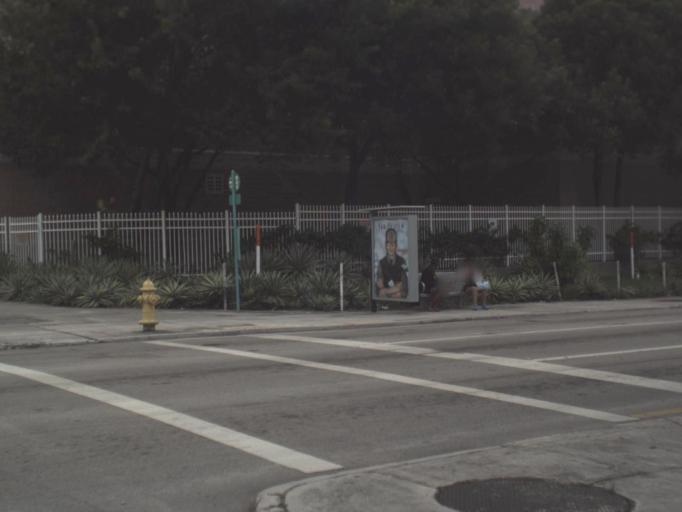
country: US
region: Florida
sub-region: Miami-Dade County
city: Miami
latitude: 25.7800
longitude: -80.1937
